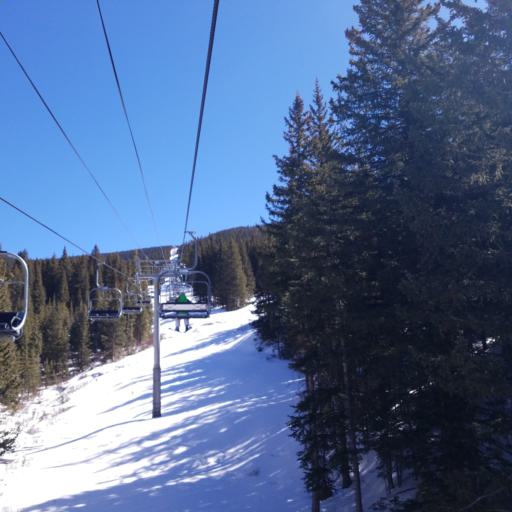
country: US
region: New Mexico
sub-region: Santa Fe County
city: Santa Fe
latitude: 35.7919
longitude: -105.7935
